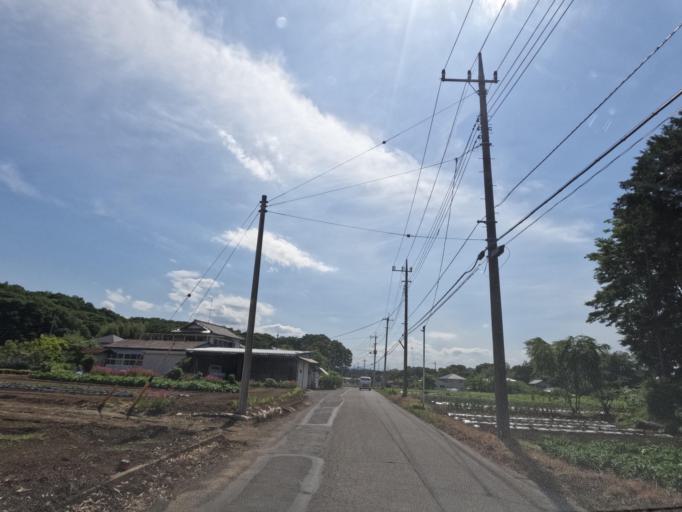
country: JP
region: Saitama
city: Kumagaya
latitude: 36.1023
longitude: 139.3804
